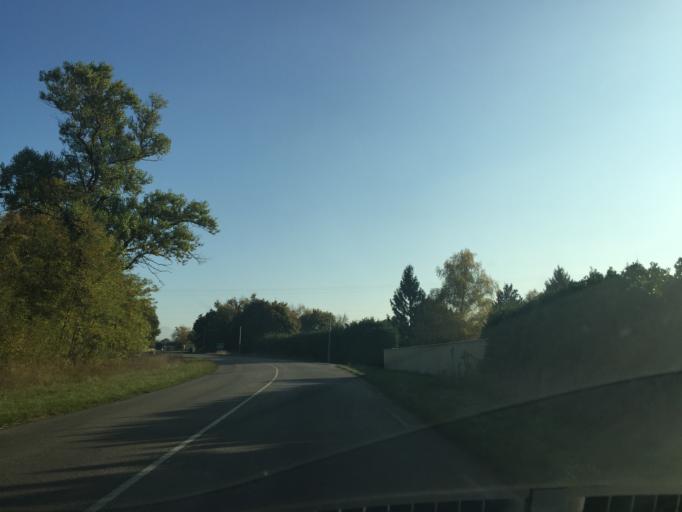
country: FR
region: Rhone-Alpes
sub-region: Departement de la Drome
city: Bourg-de-Peage
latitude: 45.0256
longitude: 5.0749
